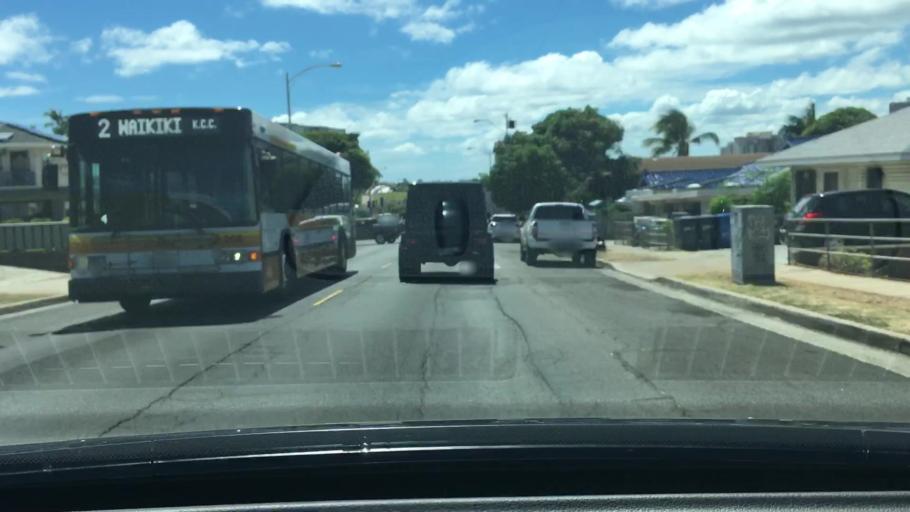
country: US
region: Hawaii
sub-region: Honolulu County
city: Honolulu
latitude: 21.2697
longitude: -157.8101
